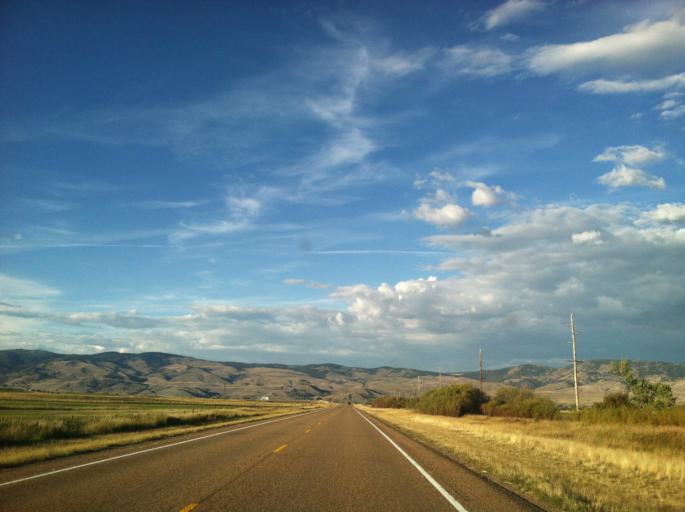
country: US
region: Montana
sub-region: Granite County
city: Philipsburg
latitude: 46.6162
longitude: -113.1759
